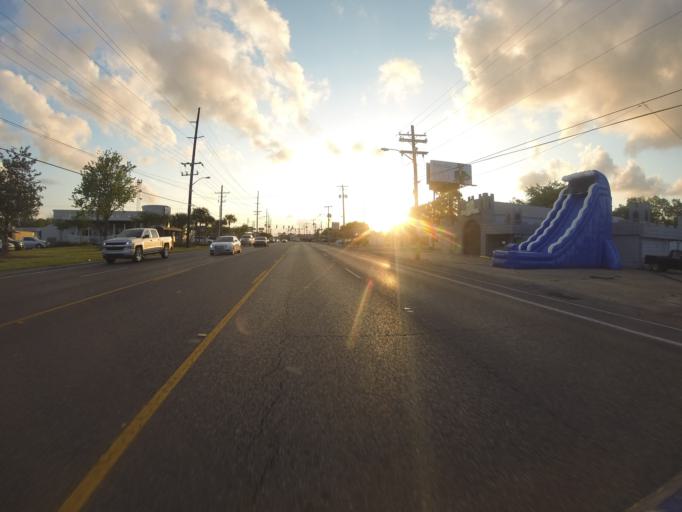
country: US
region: Louisiana
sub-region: Lafayette Parish
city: Lafayette
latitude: 30.2039
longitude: -92.0470
